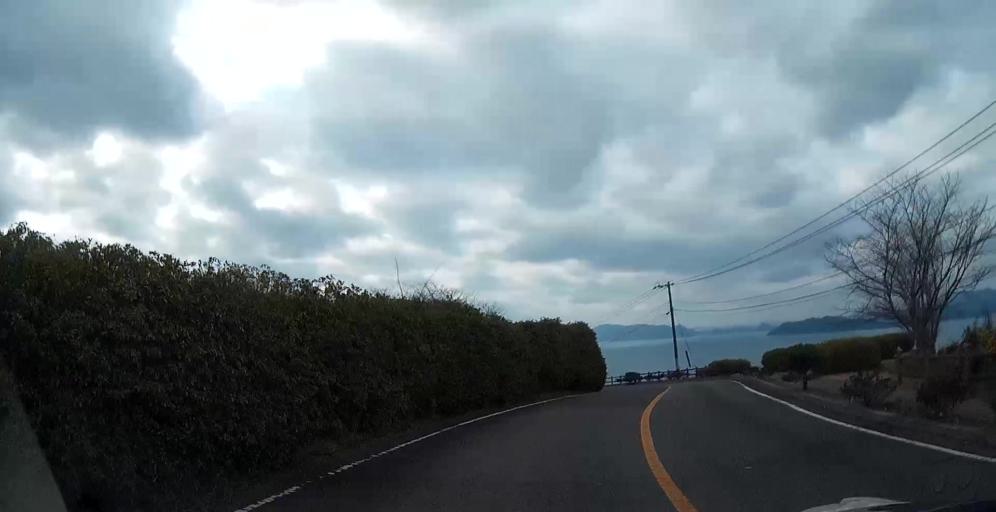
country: JP
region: Kumamoto
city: Yatsushiro
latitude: 32.3702
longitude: 130.4995
